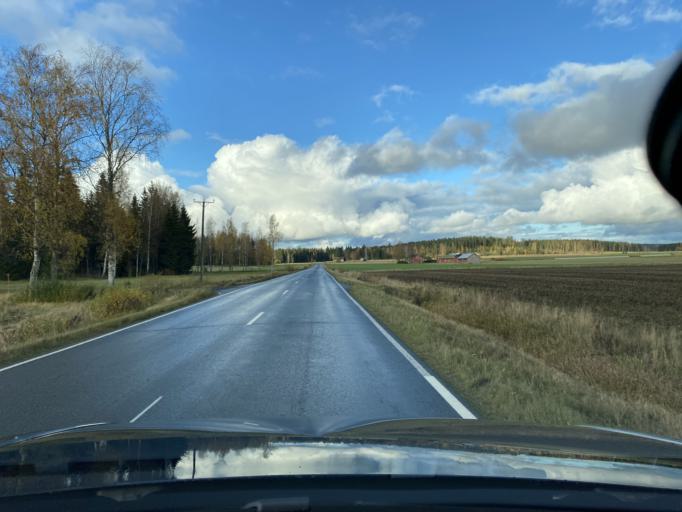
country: FI
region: Haeme
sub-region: Forssa
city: Humppila
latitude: 60.9811
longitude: 23.2532
